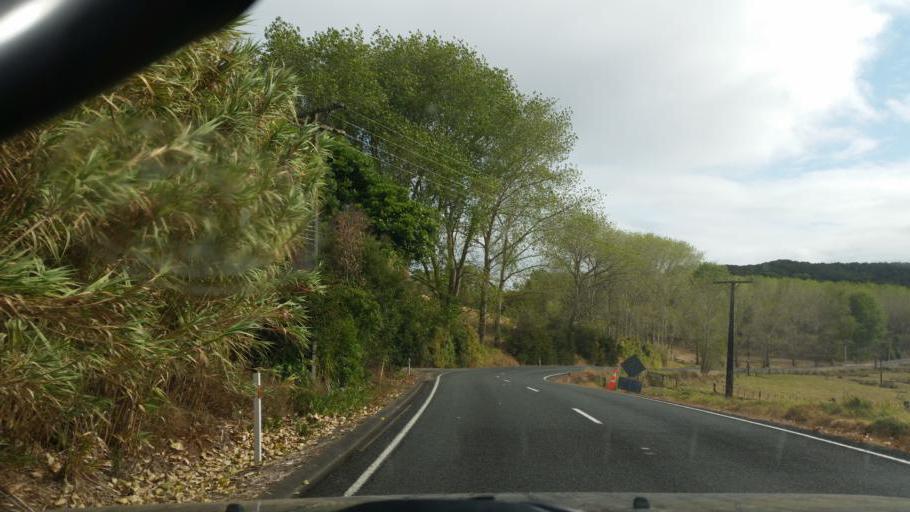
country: NZ
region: Auckland
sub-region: Auckland
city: Wellsford
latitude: -36.1978
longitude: 174.3971
